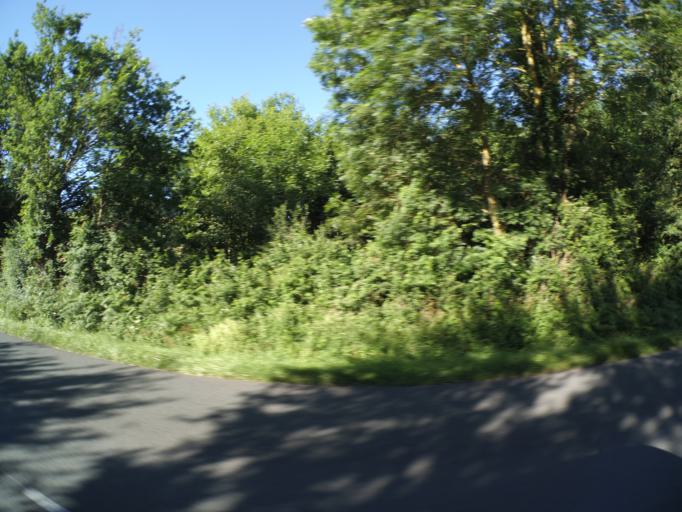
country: FR
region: Pays de la Loire
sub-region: Departement de la Vendee
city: Beaurepaire
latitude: 46.8978
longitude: -1.0656
